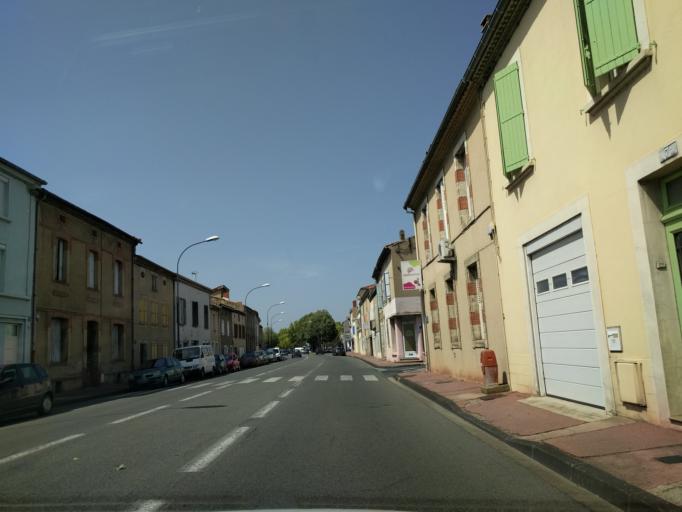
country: FR
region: Midi-Pyrenees
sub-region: Departement du Tarn
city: Castres
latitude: 43.6004
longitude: 2.2546
